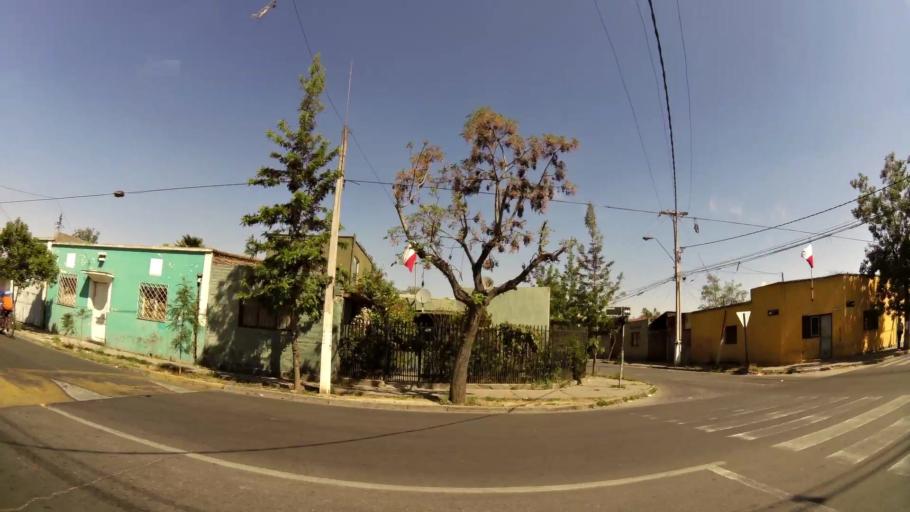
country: CL
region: Santiago Metropolitan
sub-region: Provincia de Santiago
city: Santiago
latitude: -33.5154
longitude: -70.6449
